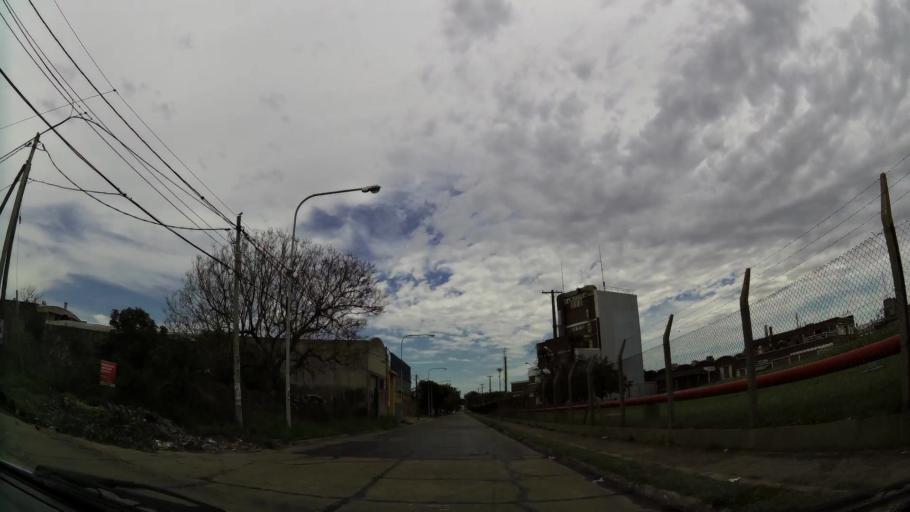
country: AR
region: Buenos Aires
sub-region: Partido de Quilmes
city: Quilmes
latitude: -34.7543
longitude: -58.2211
